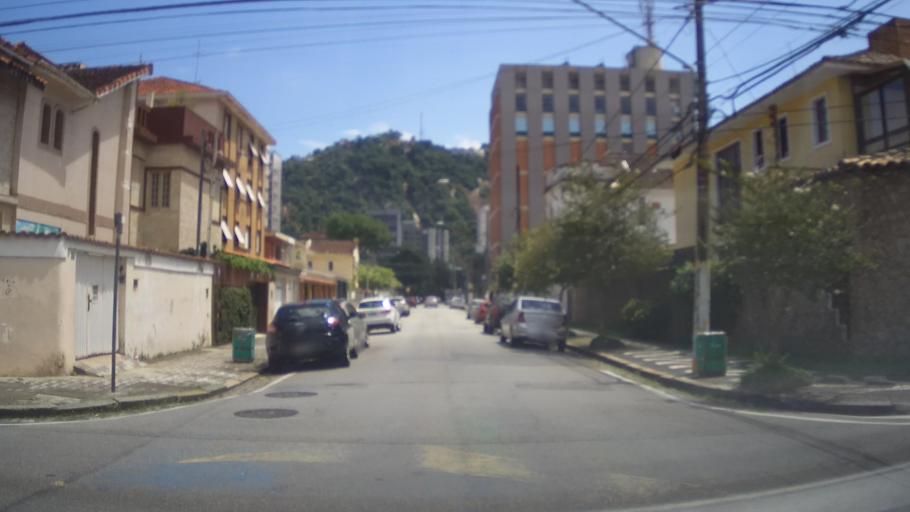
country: BR
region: Sao Paulo
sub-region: Santos
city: Santos
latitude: -23.9609
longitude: -46.3428
